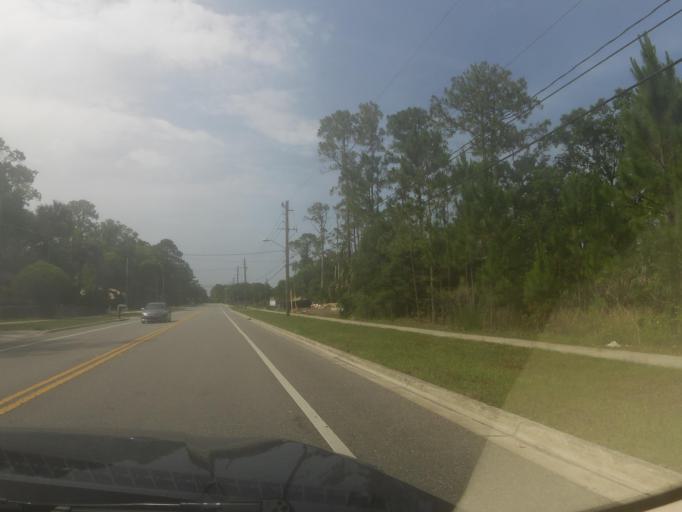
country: US
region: Florida
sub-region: Saint Johns County
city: Saint Augustine
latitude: 29.8926
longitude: -81.3447
